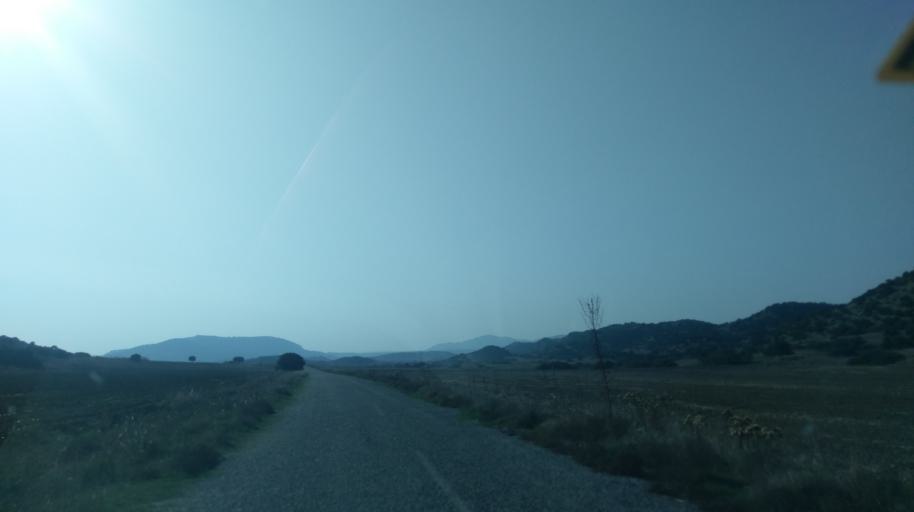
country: CY
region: Ammochostos
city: Rizokarpaso
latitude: 35.5509
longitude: 34.3538
